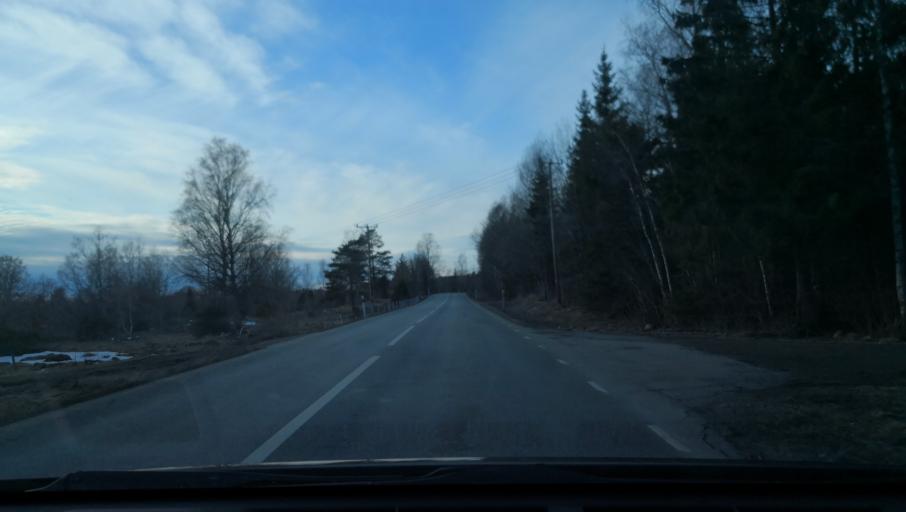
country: SE
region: Uppsala
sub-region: Osthammars Kommun
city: Gimo
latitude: 60.3369
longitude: 18.2211
